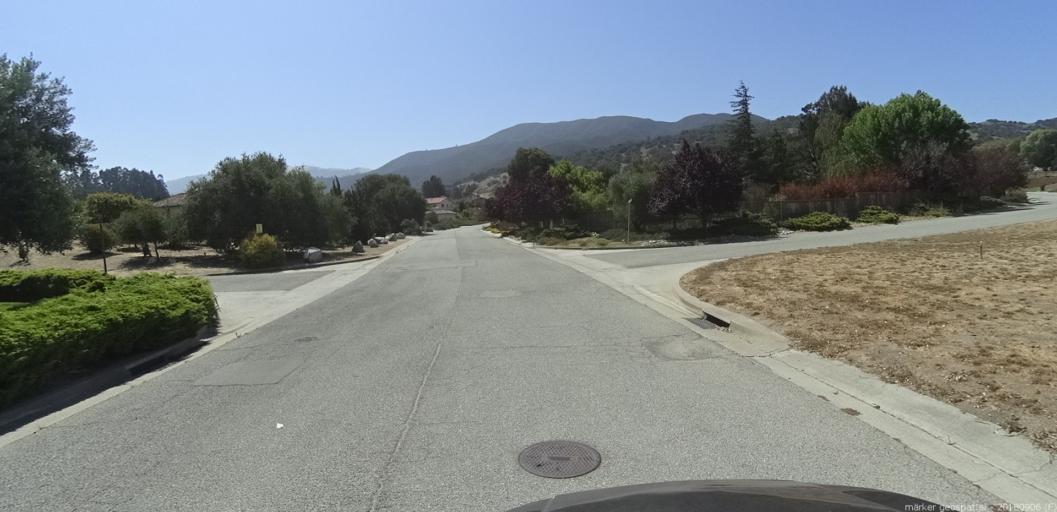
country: US
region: California
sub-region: Monterey County
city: Salinas
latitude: 36.6023
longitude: -121.6433
